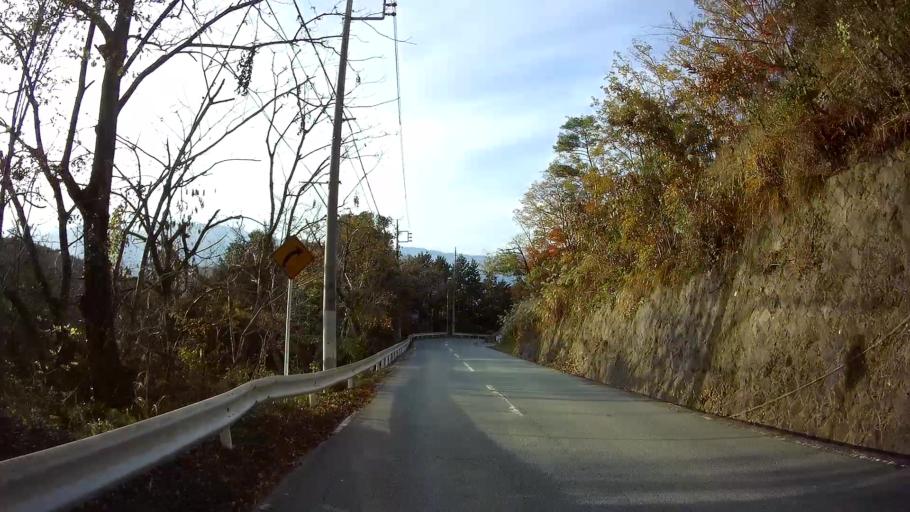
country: JP
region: Yamanashi
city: Ryuo
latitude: 35.4737
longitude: 138.4850
